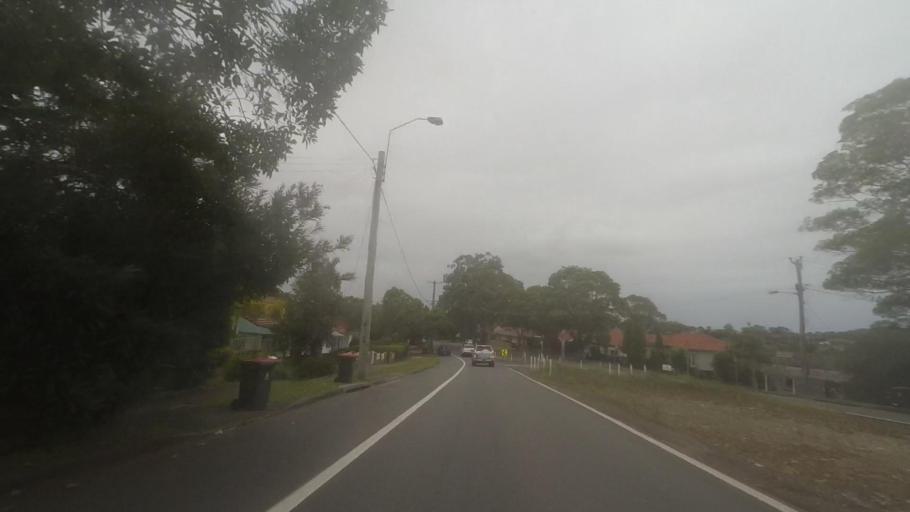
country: AU
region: New South Wales
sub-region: Lake Macquarie Shire
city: Highfields
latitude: -32.9471
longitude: 151.7146
